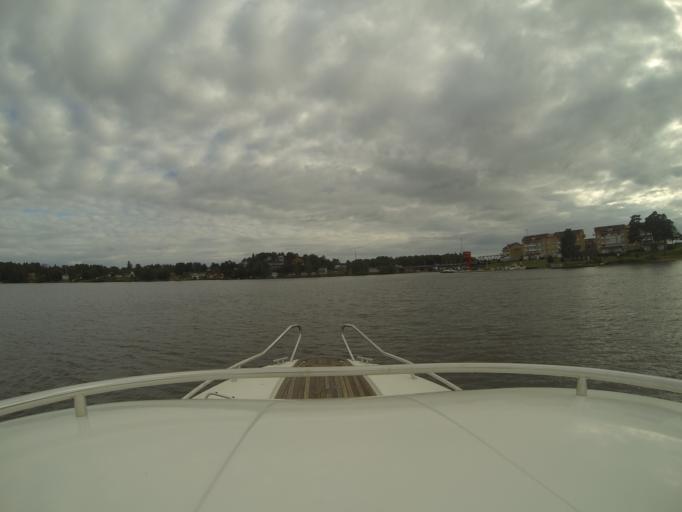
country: SE
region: Soedermanland
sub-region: Eskilstuna Kommun
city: Kvicksund
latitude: 59.4546
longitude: 16.3230
